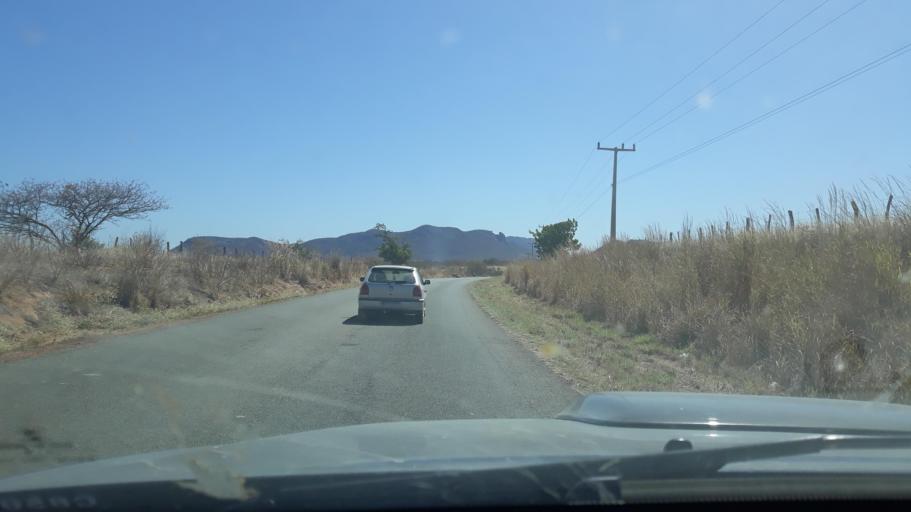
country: BR
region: Bahia
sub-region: Guanambi
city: Guanambi
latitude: -14.1744
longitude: -42.8020
